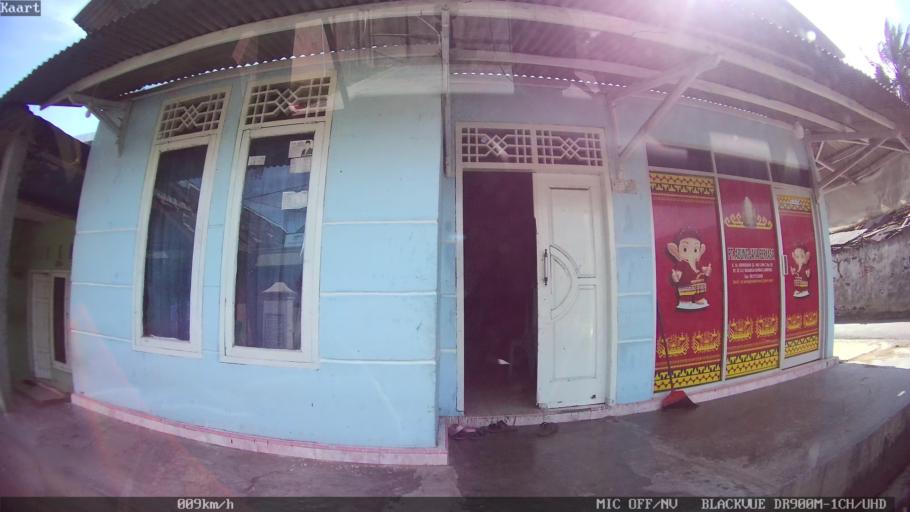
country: ID
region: Lampung
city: Kedaton
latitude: -5.3582
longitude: 105.2396
